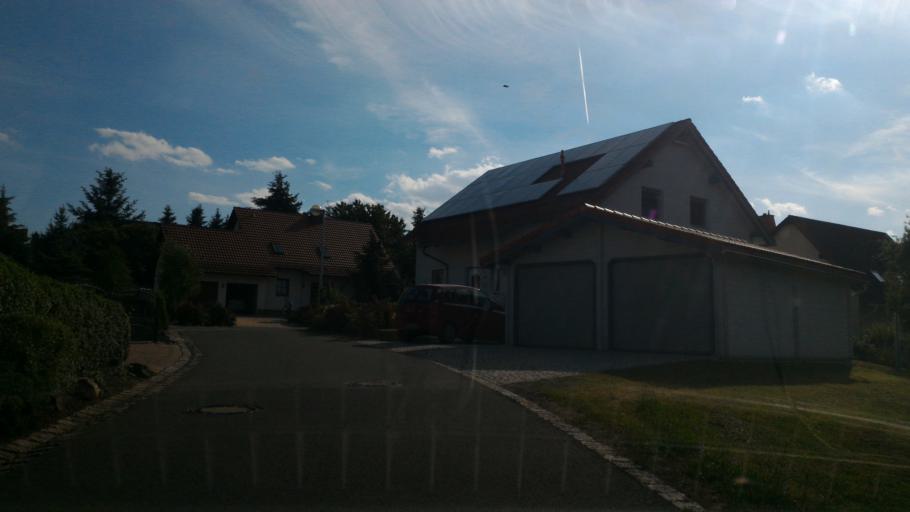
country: DE
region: Saxony
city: Olbersdorf
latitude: 50.8609
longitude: 14.7953
